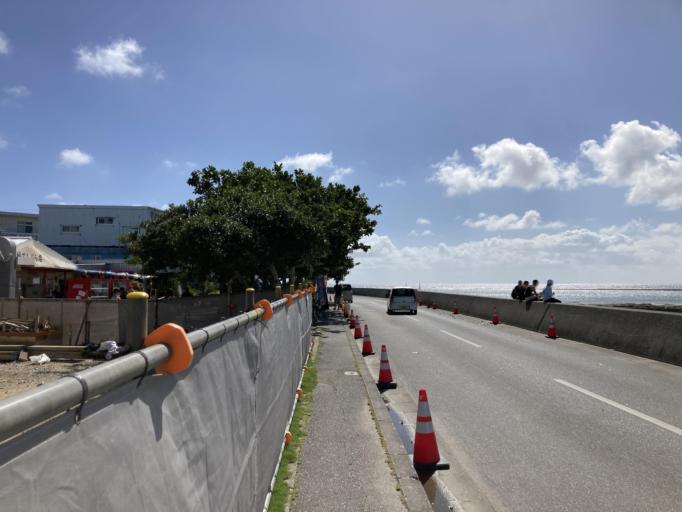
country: JP
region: Okinawa
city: Itoman
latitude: 26.1287
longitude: 127.7710
